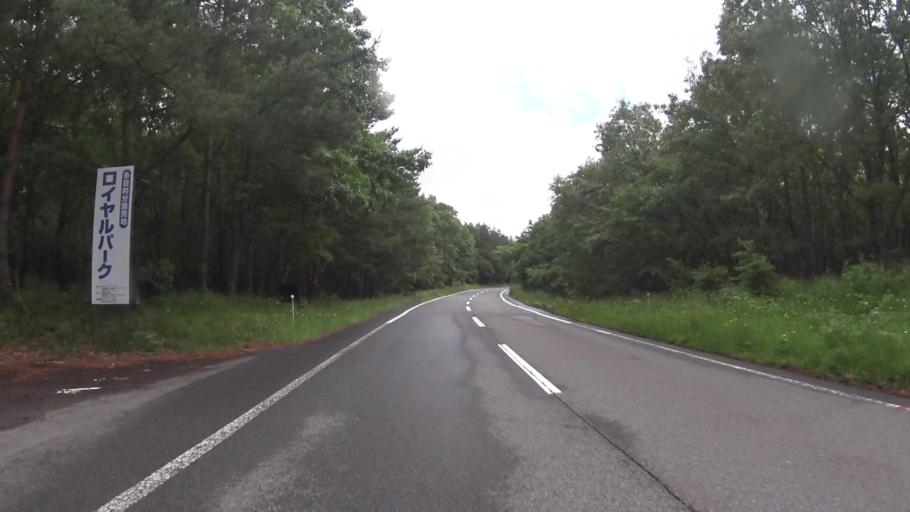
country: JP
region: Oita
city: Tsukawaki
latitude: 33.1387
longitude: 131.2403
